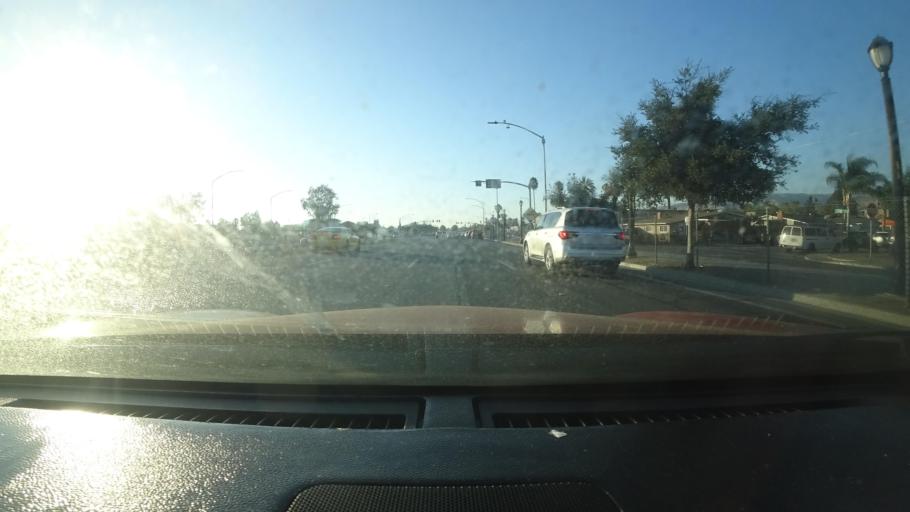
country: US
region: California
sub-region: Santa Clara County
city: Alum Rock
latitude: 37.3492
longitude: -121.8258
